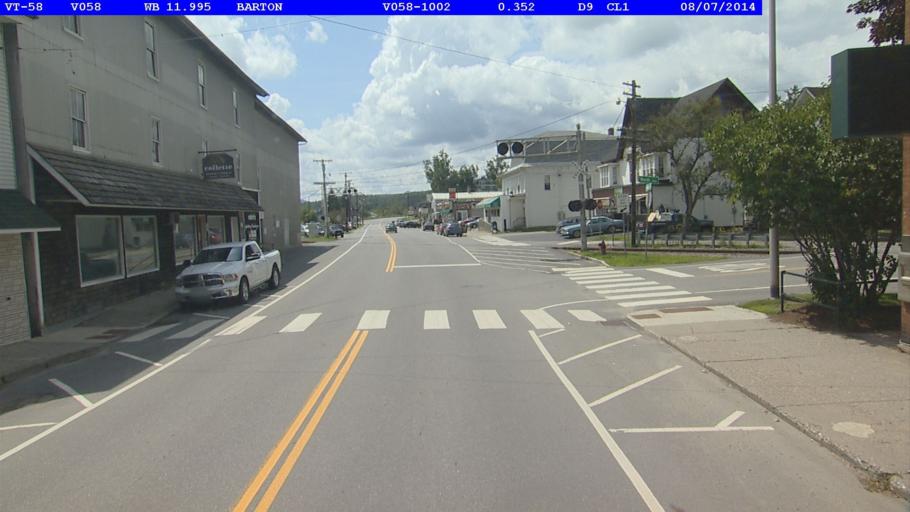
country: US
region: Vermont
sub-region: Orleans County
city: Newport
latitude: 44.8111
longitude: -72.2030
